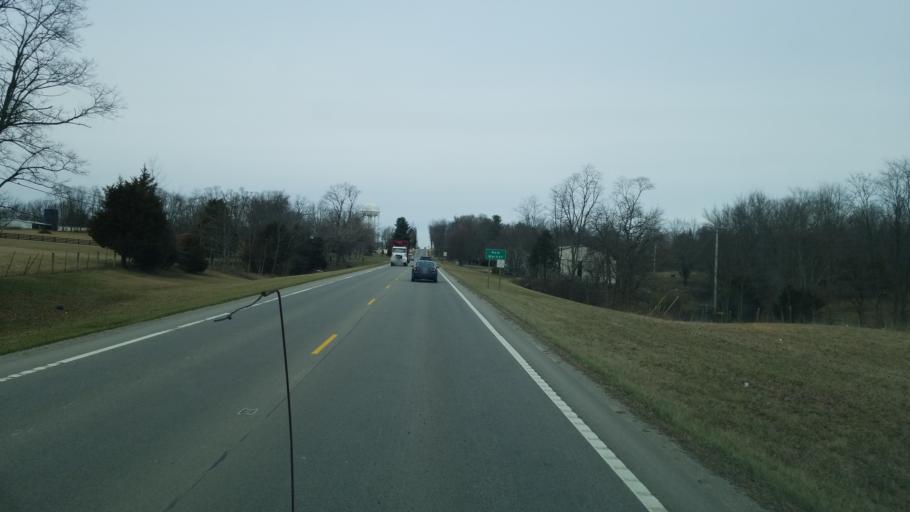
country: US
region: Ohio
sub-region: Highland County
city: Hillsboro
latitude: 39.1306
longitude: -83.6700
